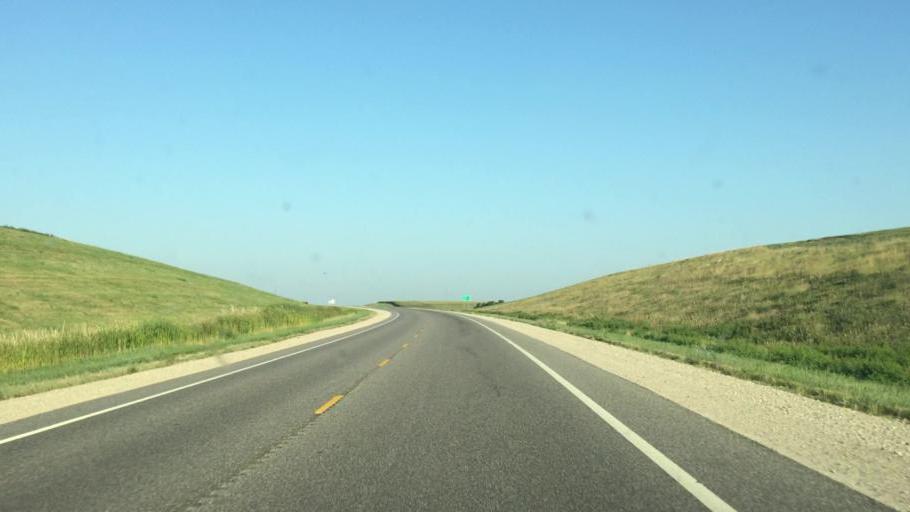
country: US
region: Kansas
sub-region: Doniphan County
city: Highland
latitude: 39.8418
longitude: -95.2766
